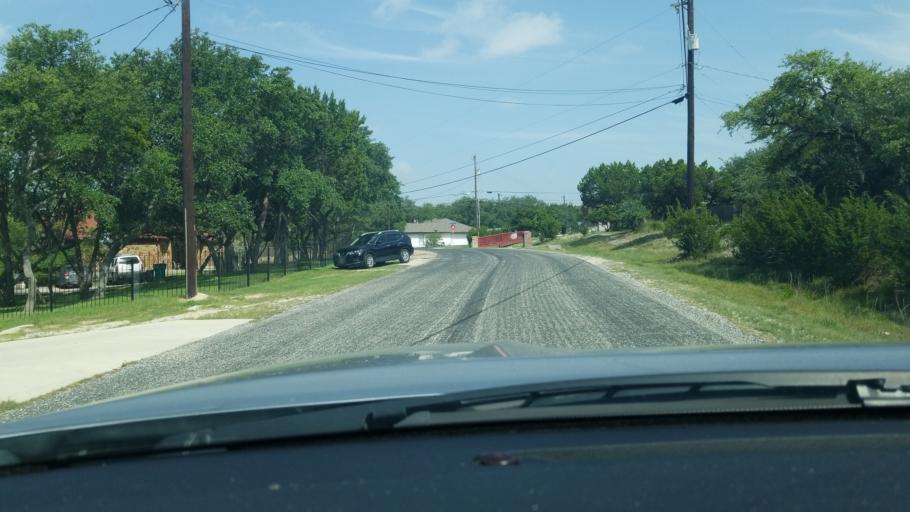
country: US
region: Texas
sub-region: Bexar County
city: Timberwood Park
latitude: 29.6922
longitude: -98.4947
